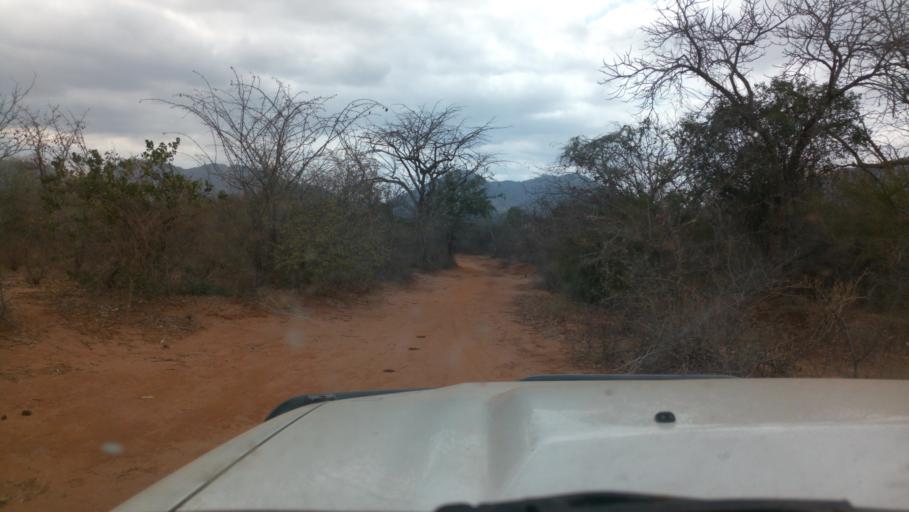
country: KE
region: Kitui
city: Kitui
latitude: -1.8636
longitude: 38.3662
